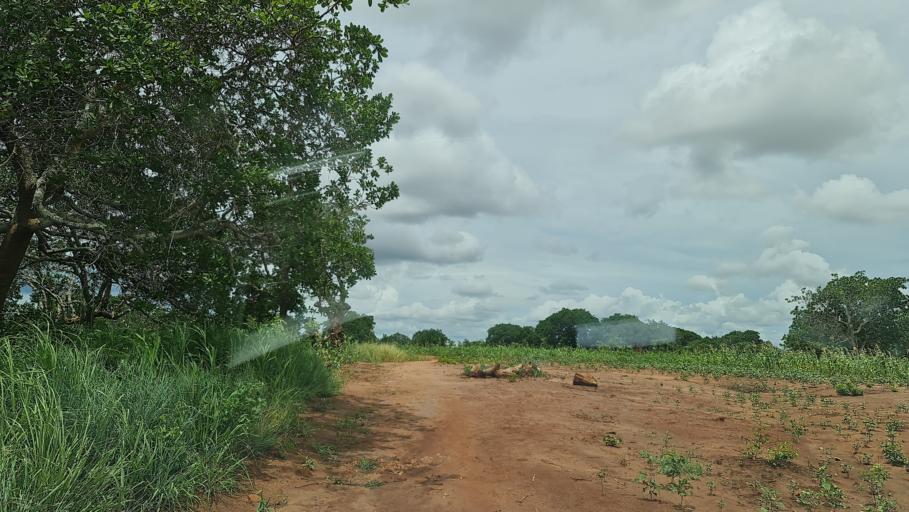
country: MZ
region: Nampula
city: Nacala
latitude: -14.7779
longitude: 39.9943
